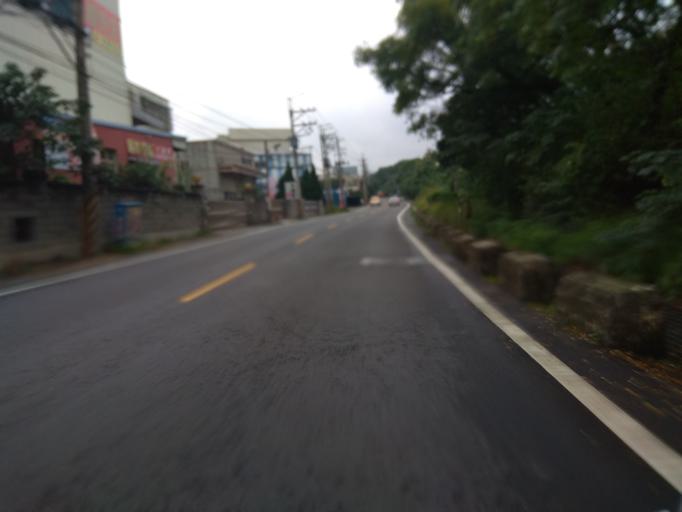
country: TW
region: Taiwan
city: Daxi
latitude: 24.9255
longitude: 121.1610
